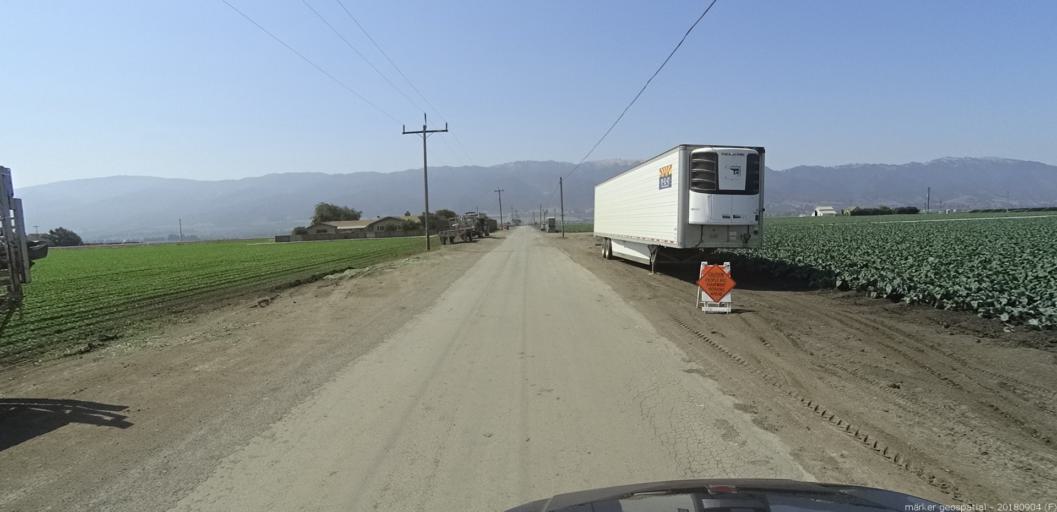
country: US
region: California
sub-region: Monterey County
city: Gonzales
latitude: 36.5153
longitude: -121.4647
